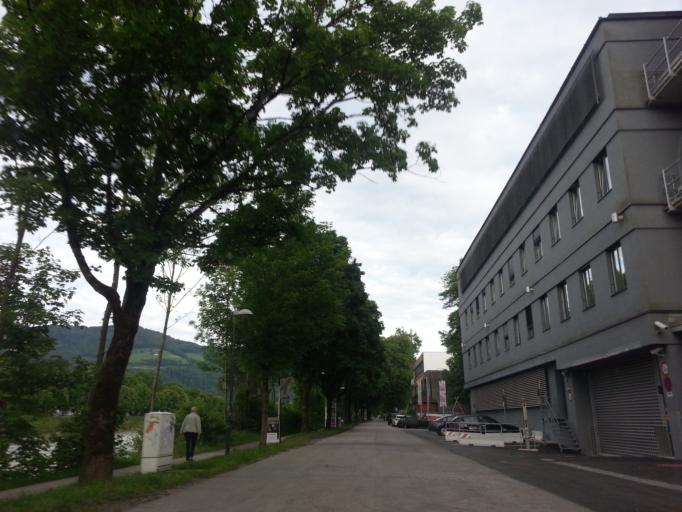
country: AT
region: Salzburg
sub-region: Salzburg Stadt
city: Salzburg
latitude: 47.7936
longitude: 13.0614
